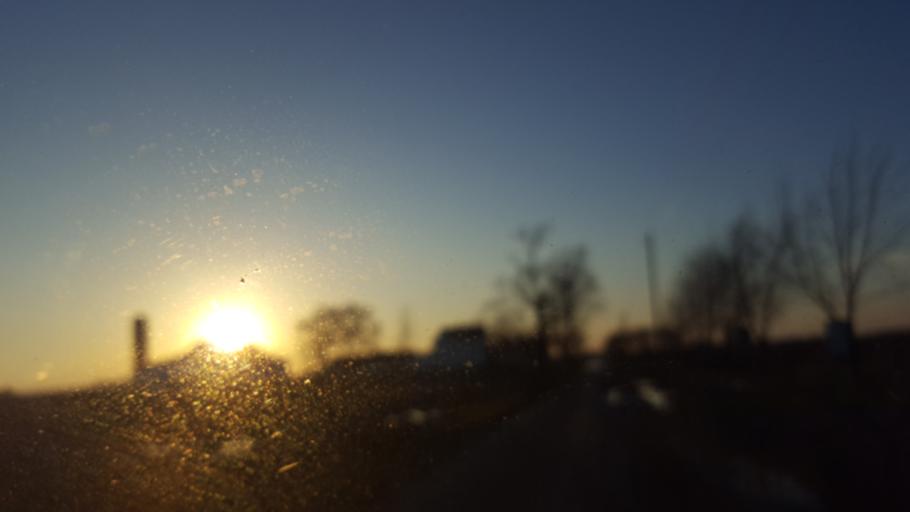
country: US
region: Indiana
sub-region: Elkhart County
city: Nappanee
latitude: 41.3843
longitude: -86.0300
